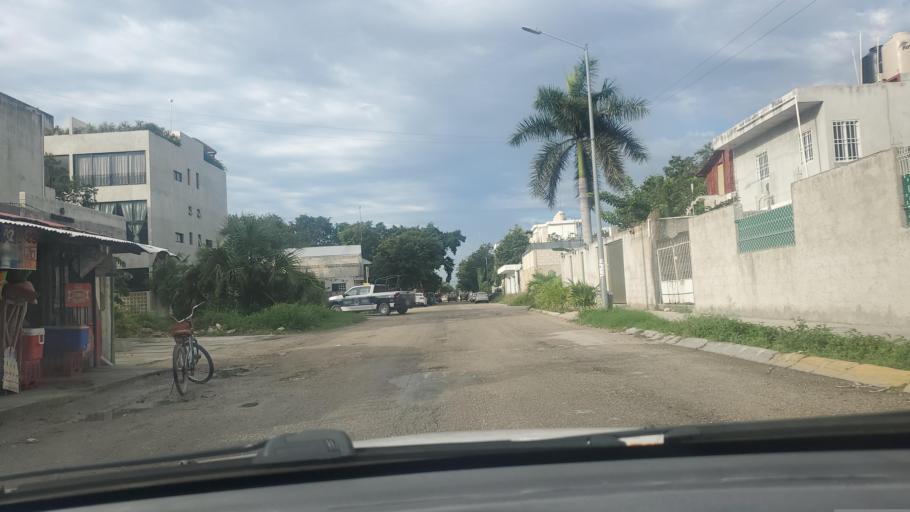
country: MX
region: Quintana Roo
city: Tulum
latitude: 20.2145
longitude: -87.4572
